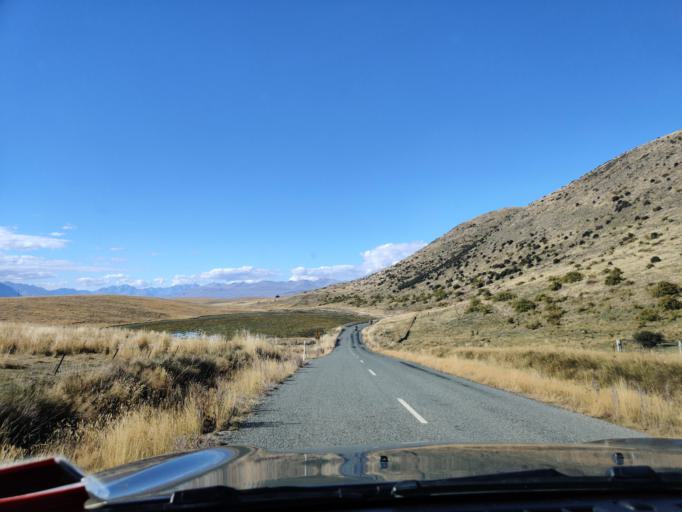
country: NZ
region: Canterbury
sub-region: Timaru District
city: Pleasant Point
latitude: -43.9805
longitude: 170.4602
